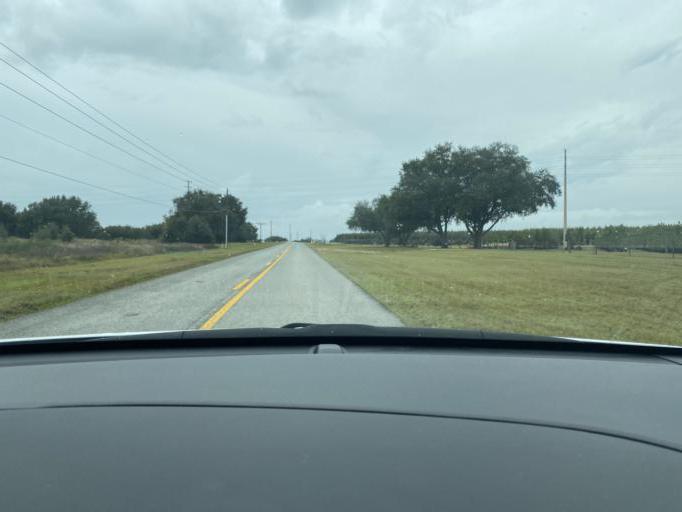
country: US
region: Florida
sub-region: Lake County
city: Groveland
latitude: 28.5890
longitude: -81.8377
